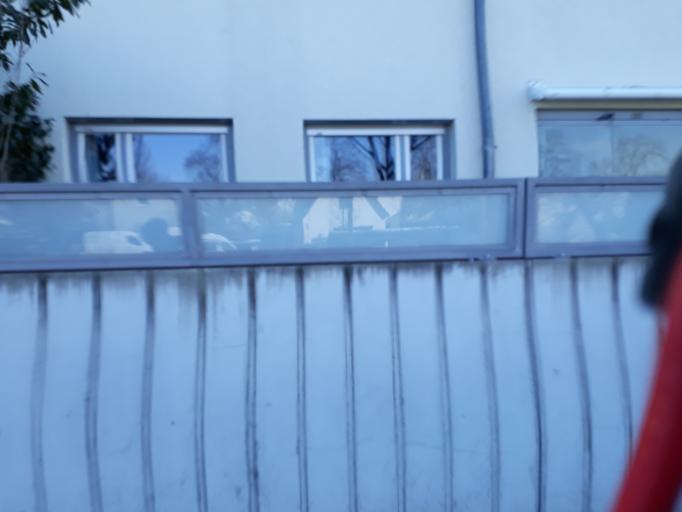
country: DE
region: Bavaria
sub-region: Upper Bavaria
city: Oberschleissheim
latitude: 48.2110
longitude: 11.5631
